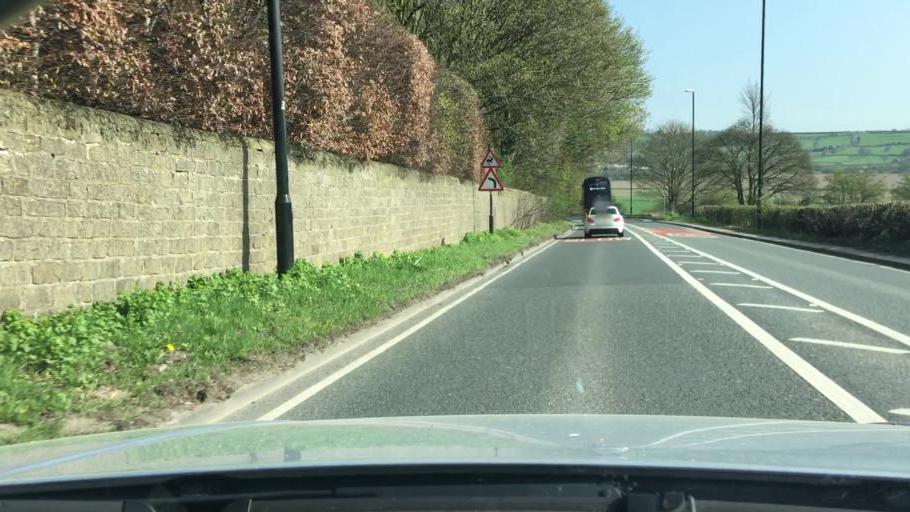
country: GB
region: England
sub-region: City and Borough of Leeds
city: East Keswick
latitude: 53.9046
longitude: -1.5112
